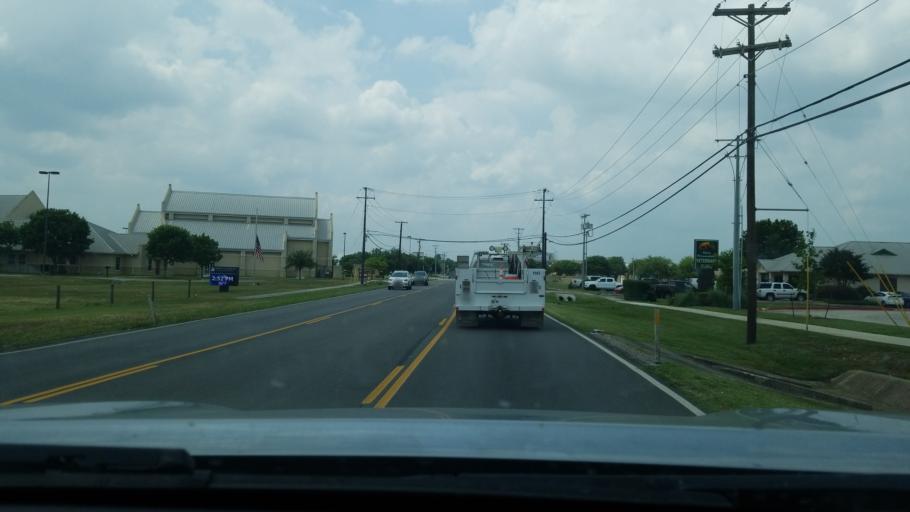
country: US
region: Texas
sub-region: Comal County
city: New Braunfels
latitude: 29.7287
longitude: -98.0954
